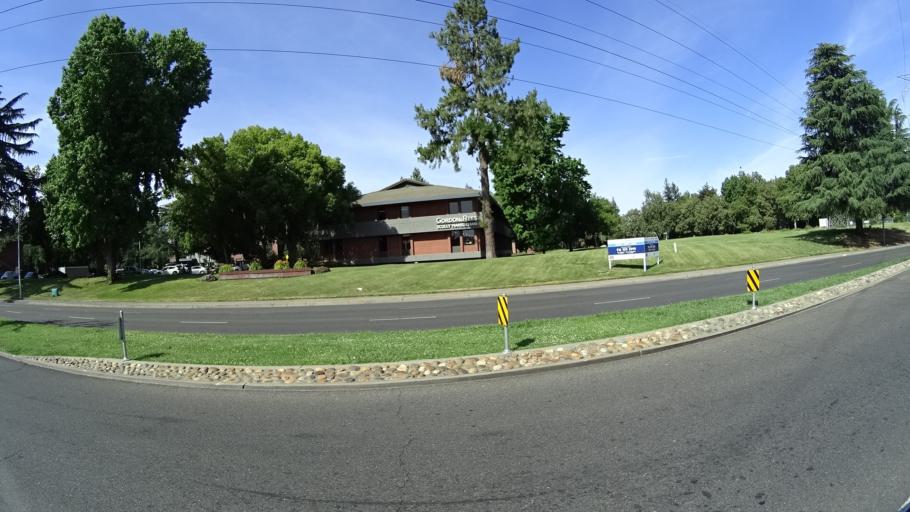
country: US
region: California
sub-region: Sacramento County
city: Arden-Arcade
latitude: 38.5731
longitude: -121.4146
